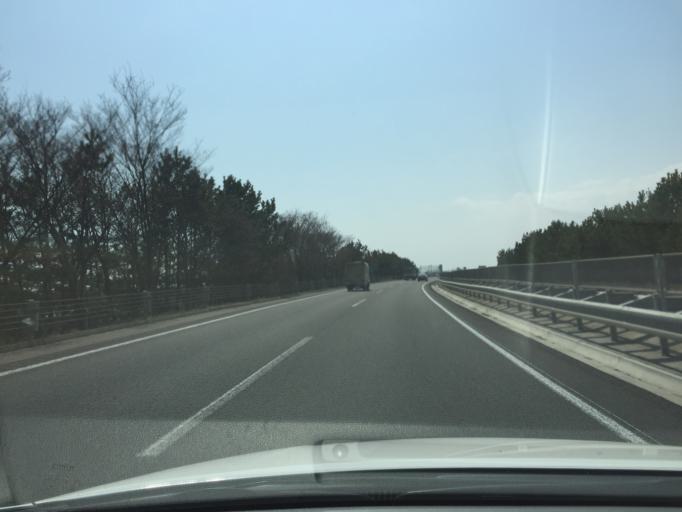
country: JP
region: Miyagi
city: Sendai-shi
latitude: 38.2310
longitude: 140.9539
